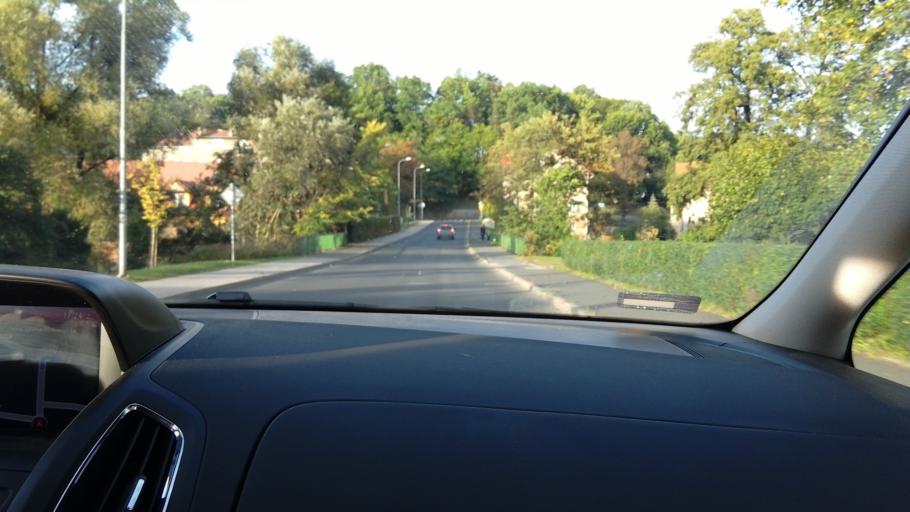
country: PL
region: Lower Silesian Voivodeship
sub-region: Jelenia Gora
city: Jelenia Gora
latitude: 50.8895
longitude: 15.7371
